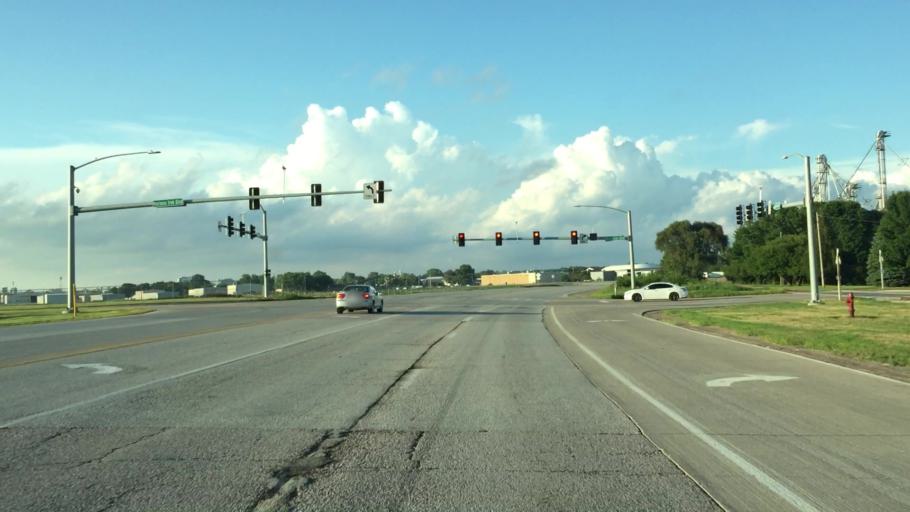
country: US
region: Iowa
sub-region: Johnson County
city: University Heights
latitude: 41.6309
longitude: -91.5427
